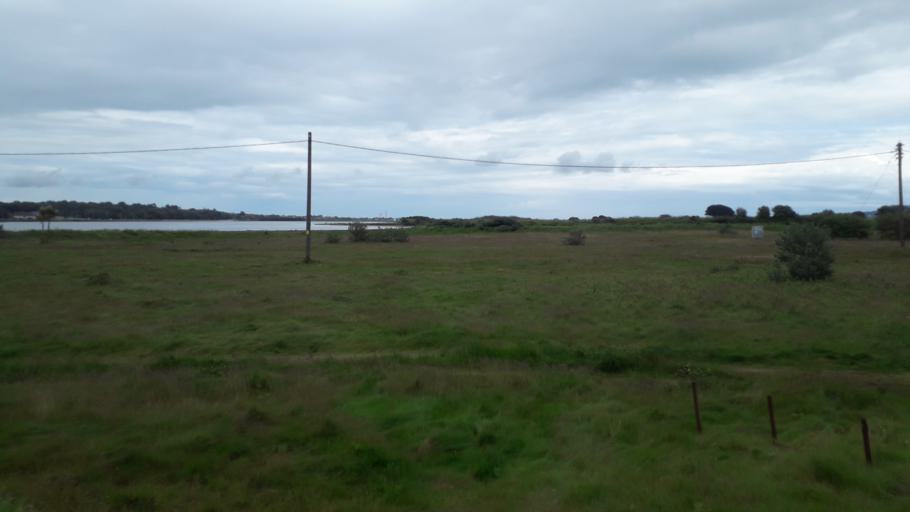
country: IE
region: Leinster
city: Dollymount
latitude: 53.3578
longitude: -6.1762
